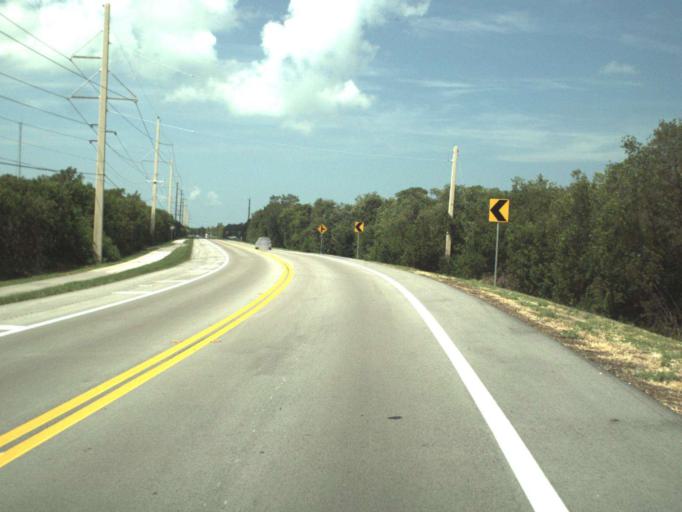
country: US
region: Florida
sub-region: Monroe County
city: Islamorada
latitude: 24.8411
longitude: -80.7883
